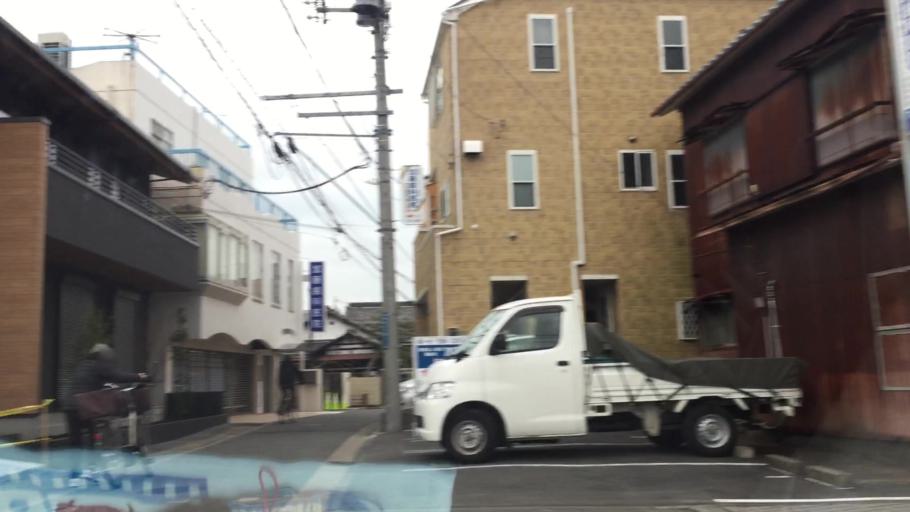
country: JP
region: Kanagawa
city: Yokosuka
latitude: 35.3380
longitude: 139.6274
